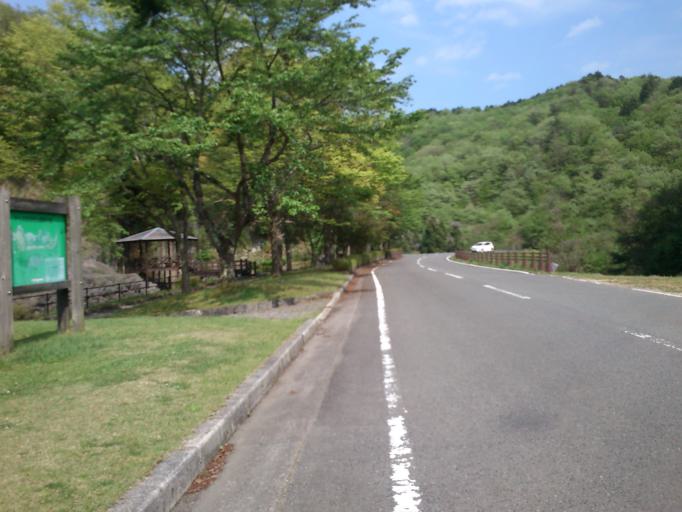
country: JP
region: Kyoto
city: Fukuchiyama
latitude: 35.3277
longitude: 134.9365
